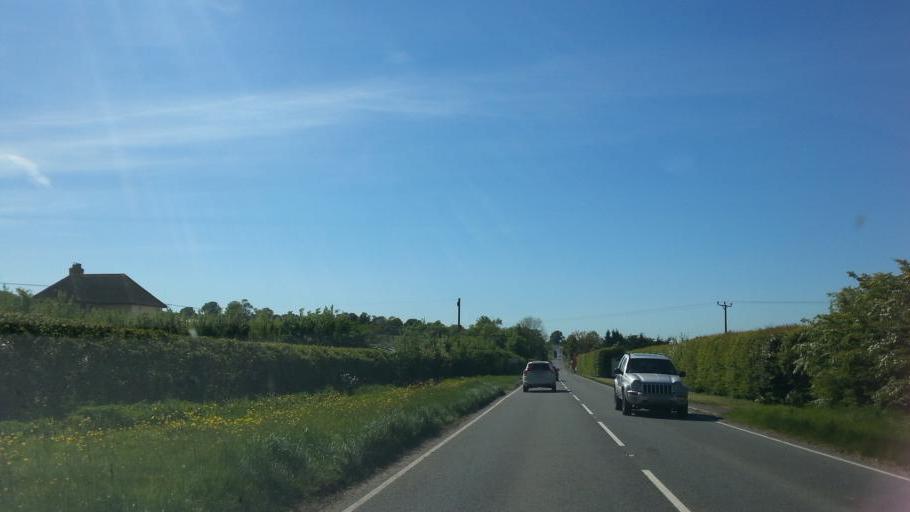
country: GB
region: England
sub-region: Dorset
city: Shaftesbury
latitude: 51.0081
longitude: -2.2343
